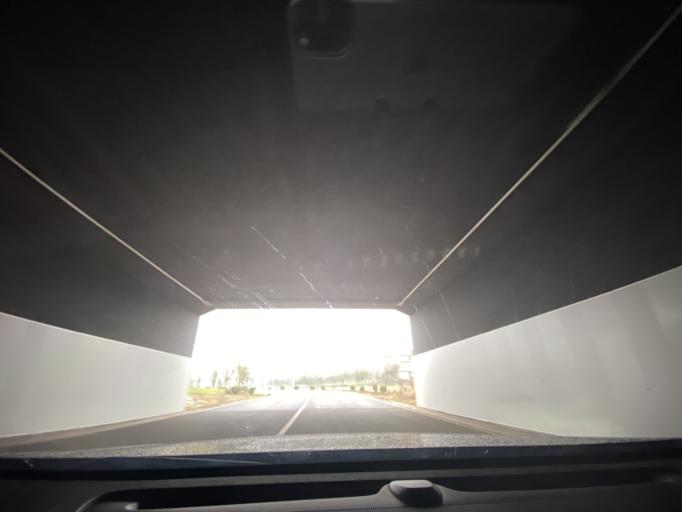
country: CN
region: Sichuan
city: Jiancheng
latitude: 30.3950
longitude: 104.6336
